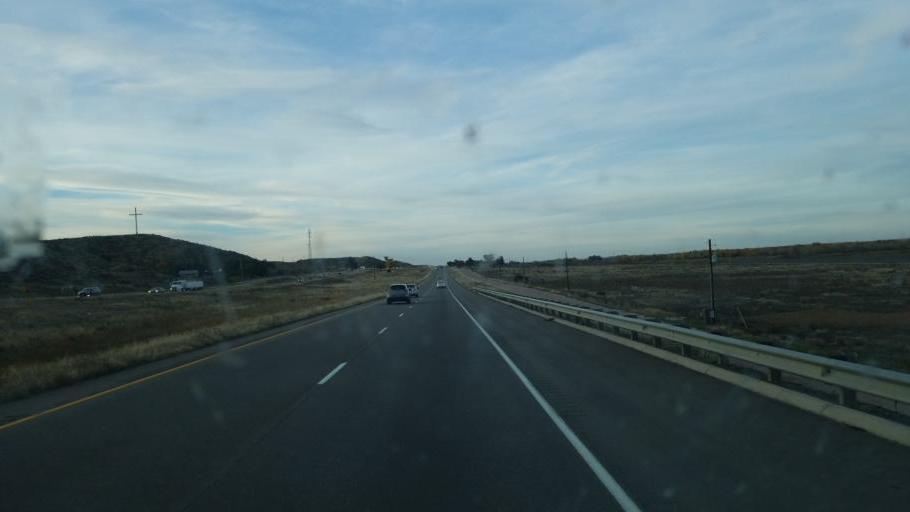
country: US
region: Colorado
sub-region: Pueblo County
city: Pueblo West
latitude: 38.4596
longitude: -104.6081
